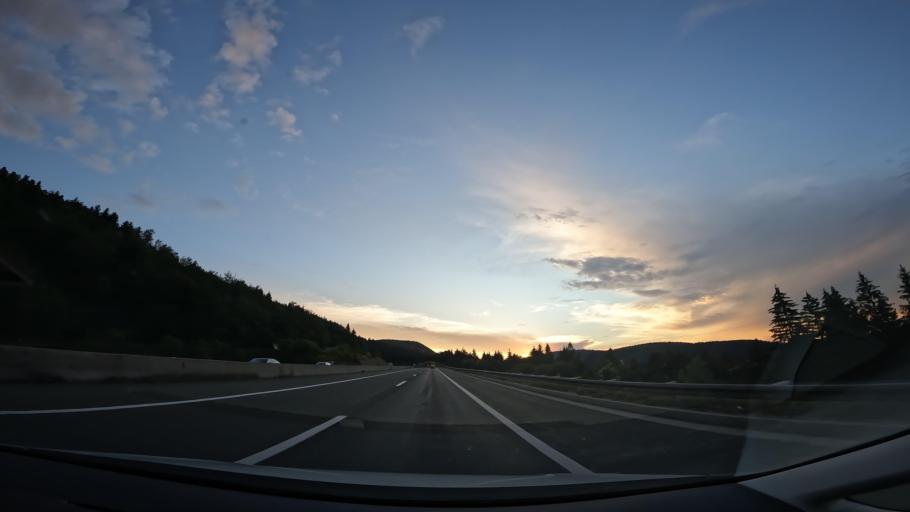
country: HR
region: Primorsko-Goranska
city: Vrbovsko
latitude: 45.3744
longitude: 14.9962
